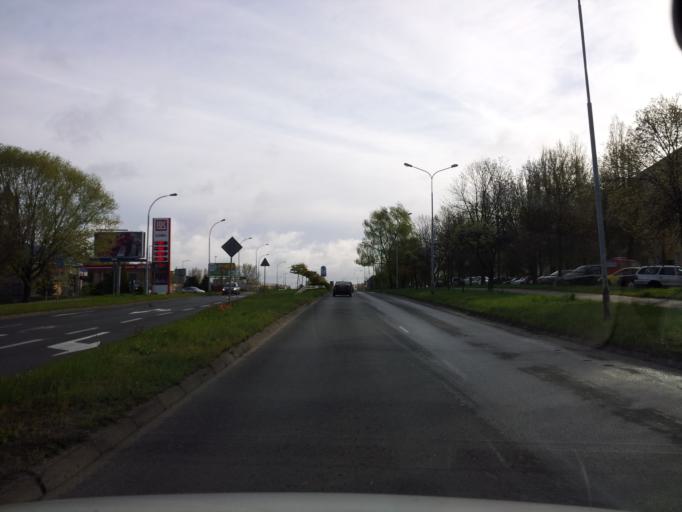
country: PL
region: Lubusz
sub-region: Zielona Gora
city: Zielona Gora
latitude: 51.9311
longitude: 15.4798
